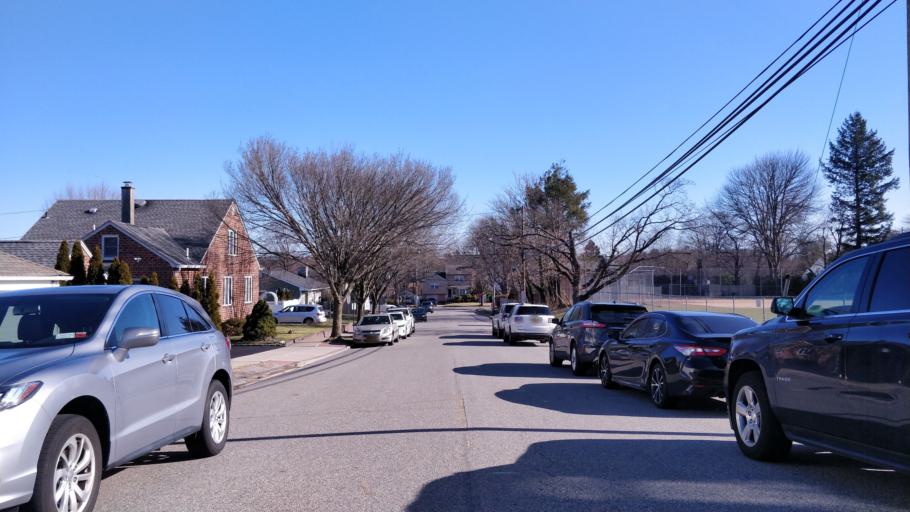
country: US
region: New York
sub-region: Nassau County
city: Glen Head
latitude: 40.8336
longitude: -73.6239
